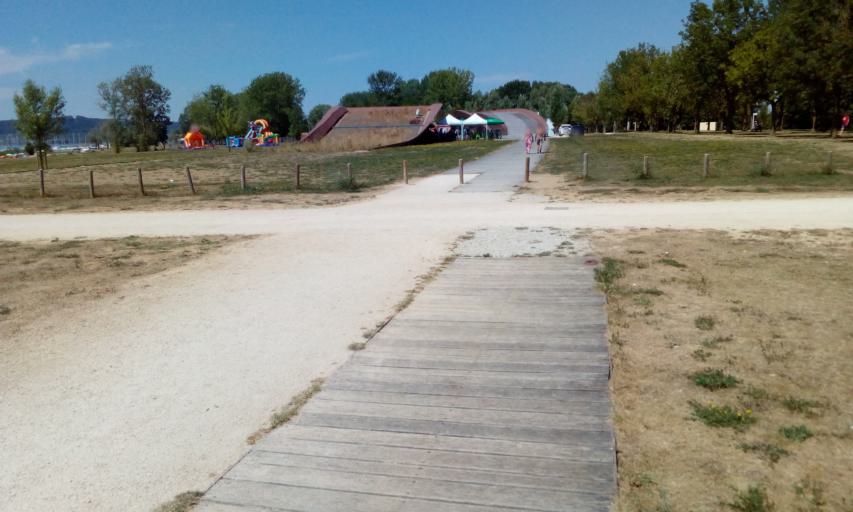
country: FR
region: Lorraine
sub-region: Departement de la Meuse
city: Vigneulles-les-Hattonchatel
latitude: 48.9263
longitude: 5.7569
